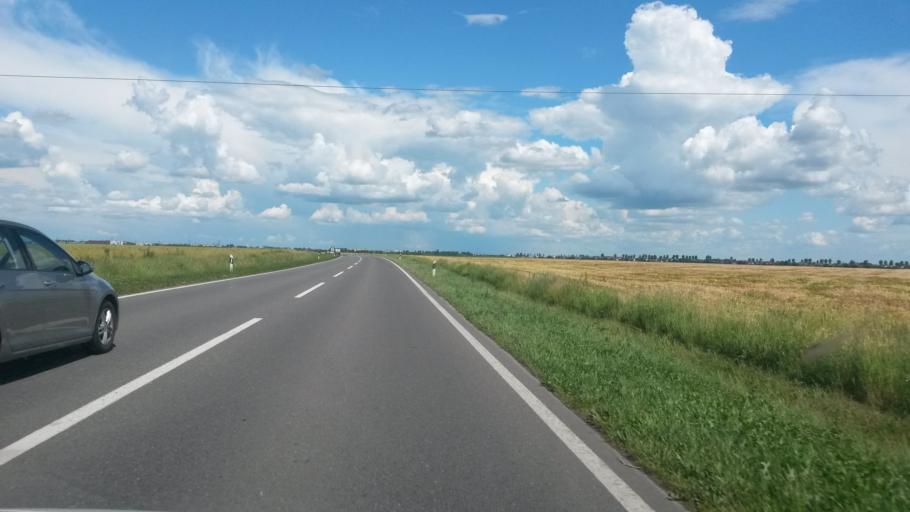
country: HR
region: Osjecko-Baranjska
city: Visnjevac
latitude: 45.5412
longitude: 18.5987
